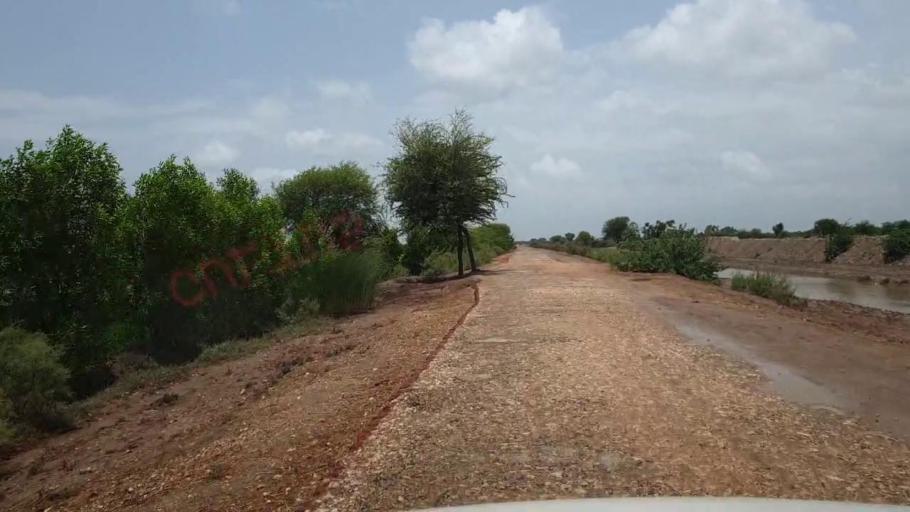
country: PK
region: Sindh
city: Kario
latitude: 24.7132
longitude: 68.5916
